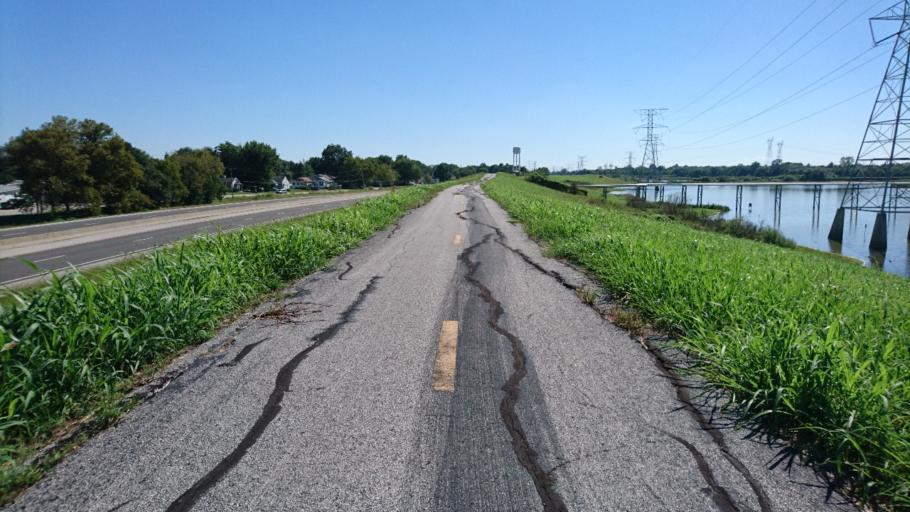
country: US
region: Illinois
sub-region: Madison County
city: Hartford
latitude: 38.8385
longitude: -90.0982
